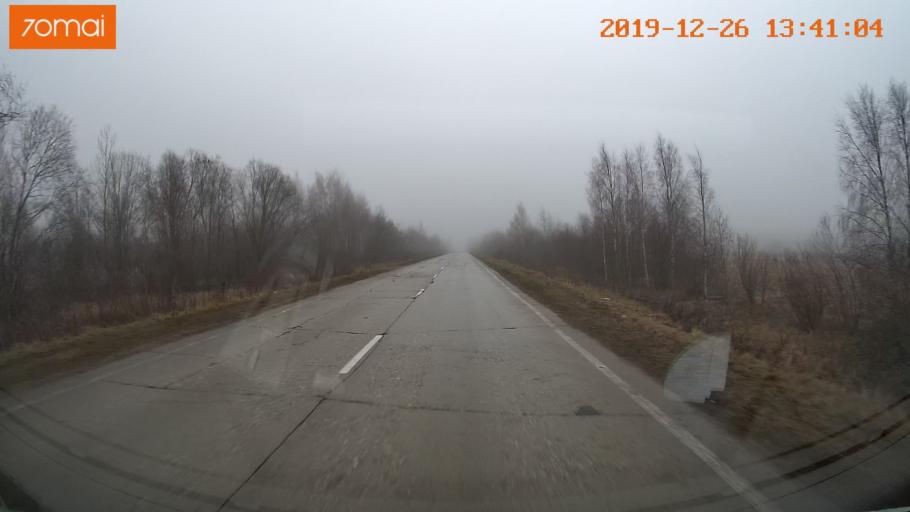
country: RU
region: Vologda
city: Sheksna
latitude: 58.7355
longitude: 38.4418
